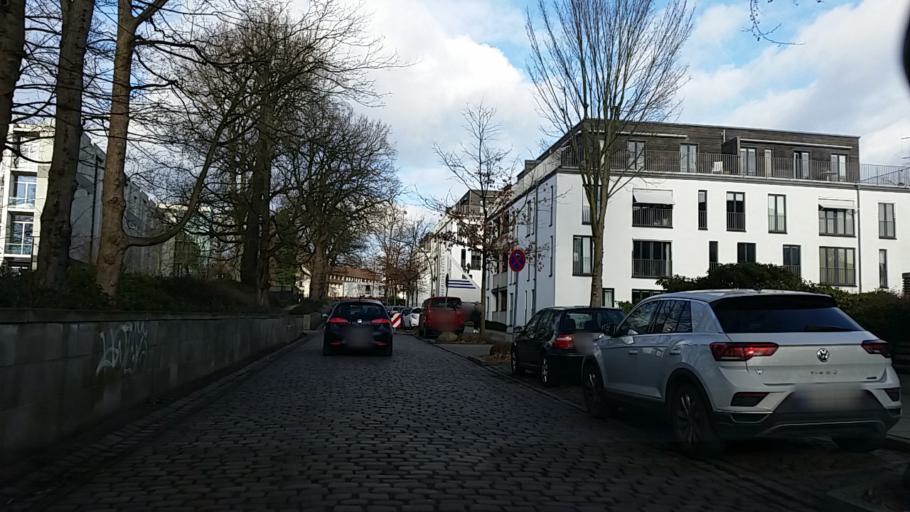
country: DE
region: Hamburg
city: Eidelstedt
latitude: 53.5501
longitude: 9.8517
